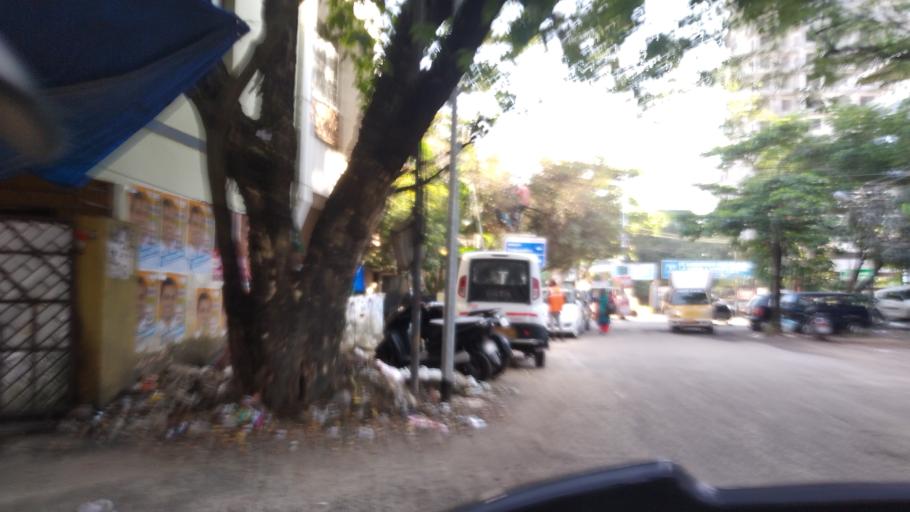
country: IN
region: Kerala
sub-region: Ernakulam
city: Cochin
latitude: 9.9902
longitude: 76.2905
